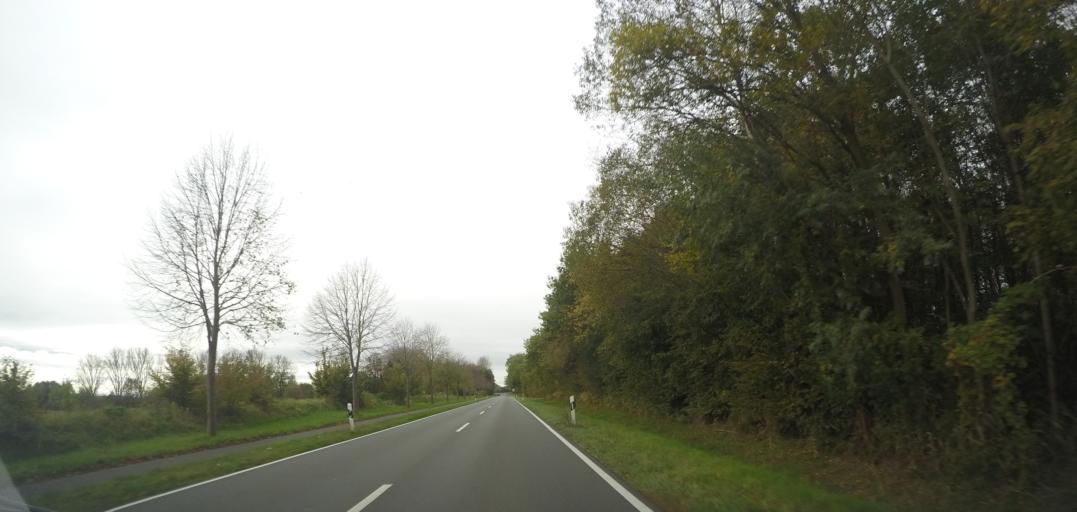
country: DE
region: North Rhine-Westphalia
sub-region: Regierungsbezirk Arnsberg
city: Lippstadt
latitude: 51.6749
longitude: 8.2840
